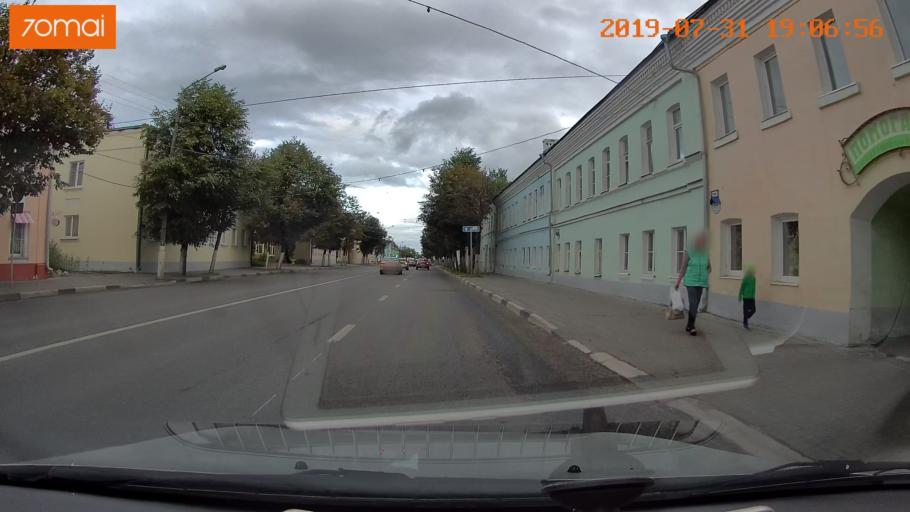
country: RU
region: Moskovskaya
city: Kolomna
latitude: 55.0998
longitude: 38.7578
